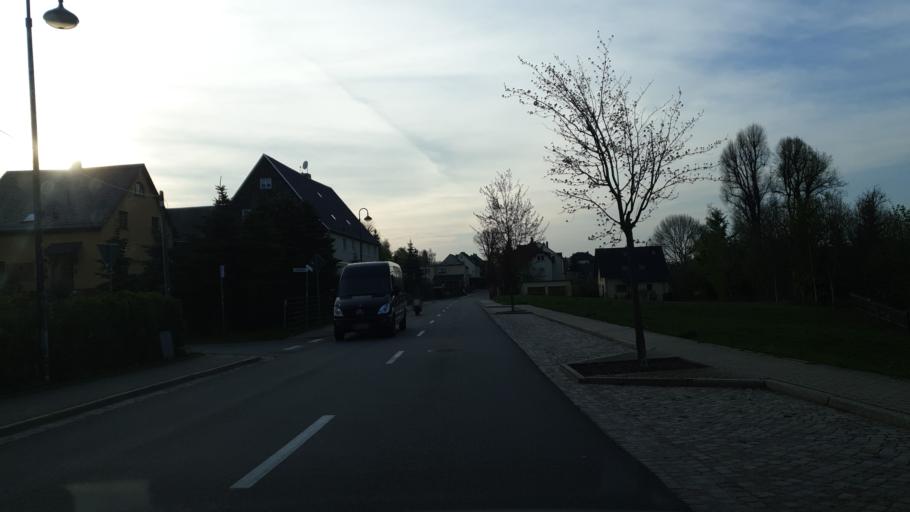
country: DE
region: Saxony
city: Lugau
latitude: 50.7389
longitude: 12.7348
